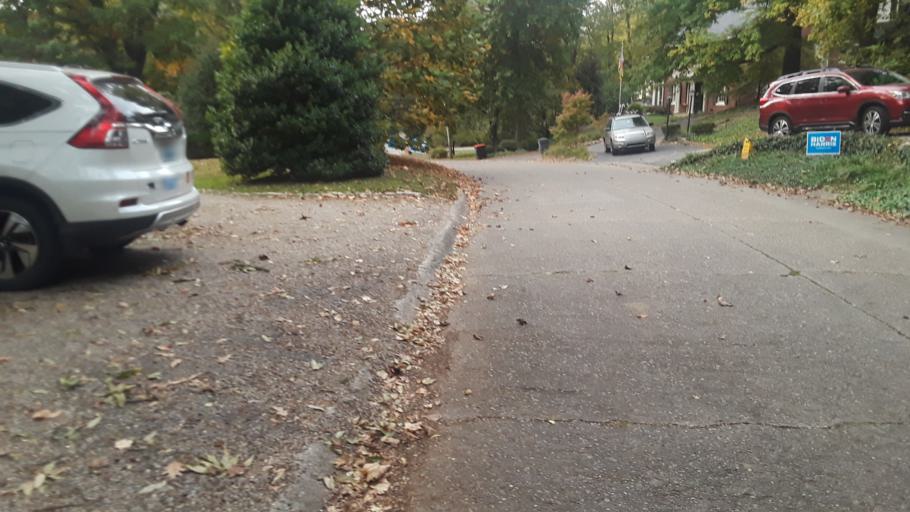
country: US
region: Kentucky
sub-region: Jefferson County
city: Saint Matthews
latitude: 38.2458
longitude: -85.6937
